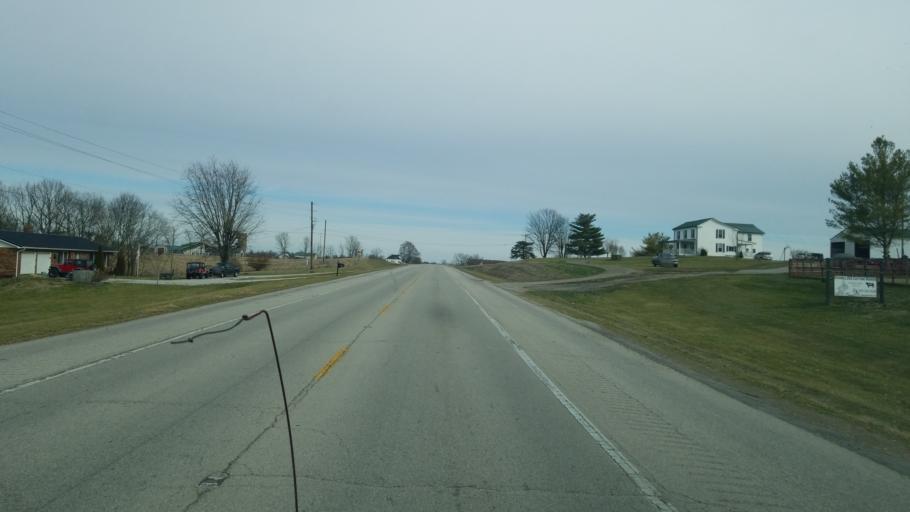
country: US
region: Kentucky
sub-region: Fleming County
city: Flemingsburg
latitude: 38.4815
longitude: -83.8721
